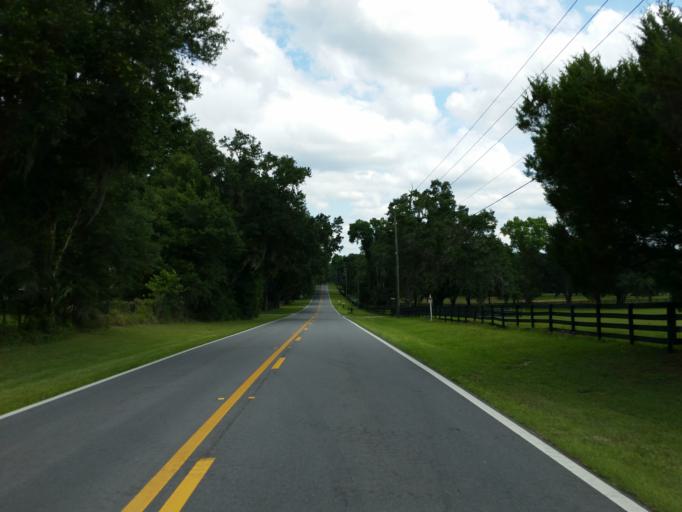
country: US
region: Florida
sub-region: Hernando County
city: North Brooksville
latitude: 28.6395
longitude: -82.3597
